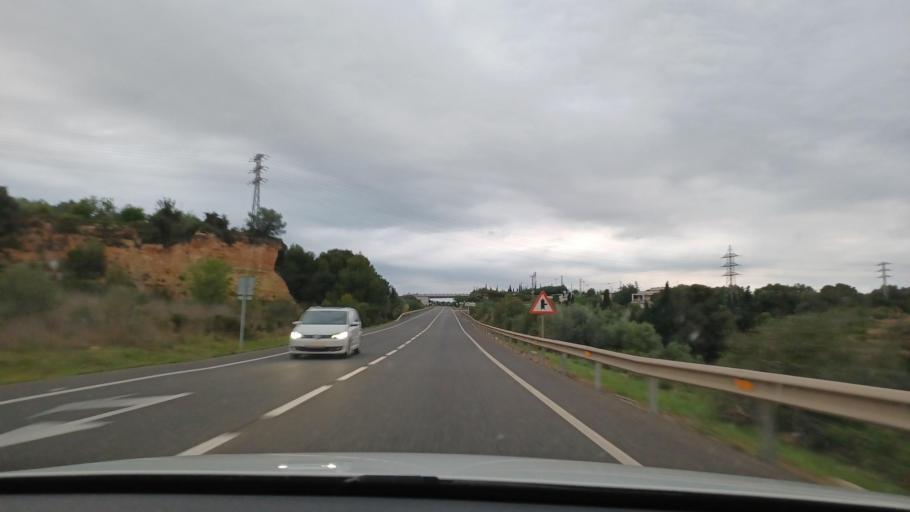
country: ES
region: Catalonia
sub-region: Provincia de Tarragona
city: Amposta
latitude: 40.7124
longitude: 0.5652
